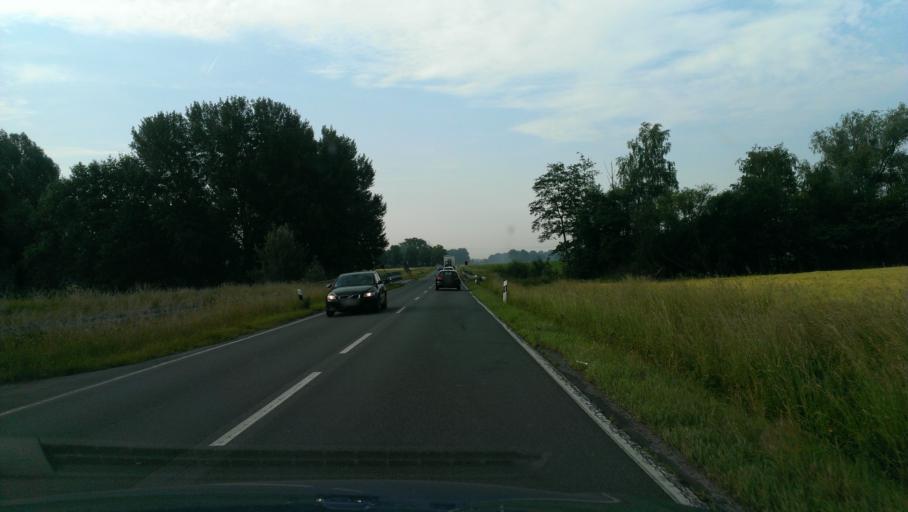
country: DE
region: North Rhine-Westphalia
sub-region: Regierungsbezirk Munster
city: Muenster
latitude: 51.9056
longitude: 7.6951
